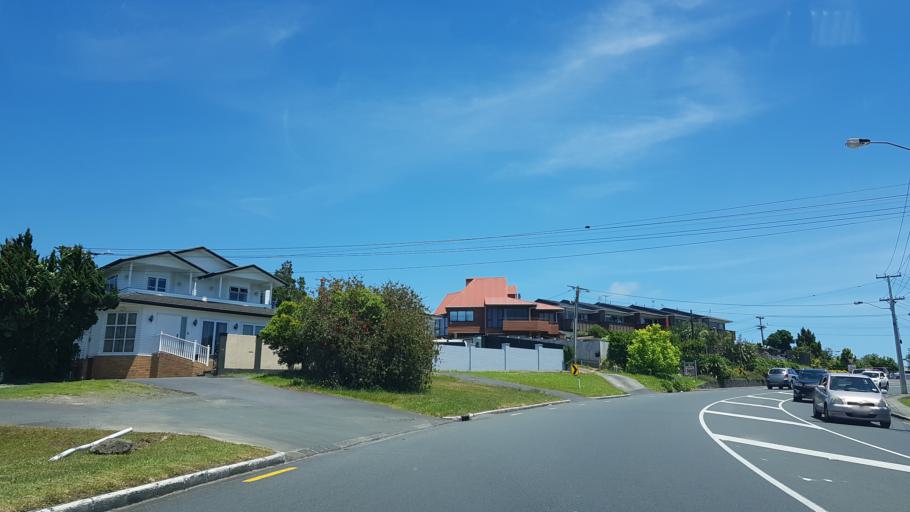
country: NZ
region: Auckland
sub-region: Auckland
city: Waitakere
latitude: -36.9129
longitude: 174.6597
